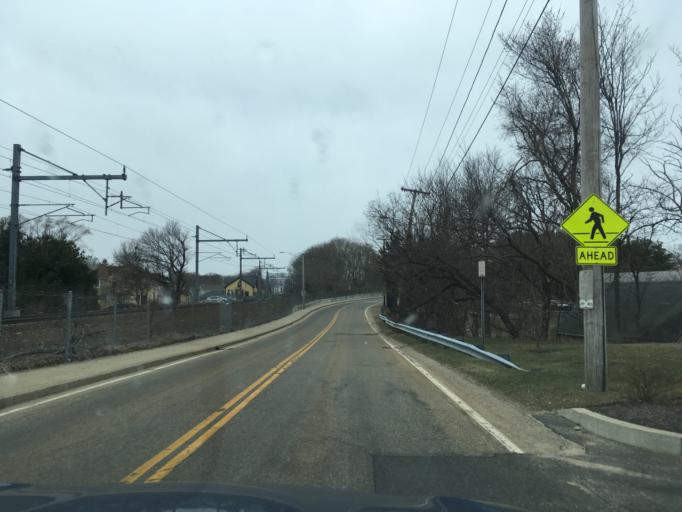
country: US
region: Rhode Island
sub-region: Kent County
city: East Greenwich
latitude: 41.6577
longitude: -71.4489
